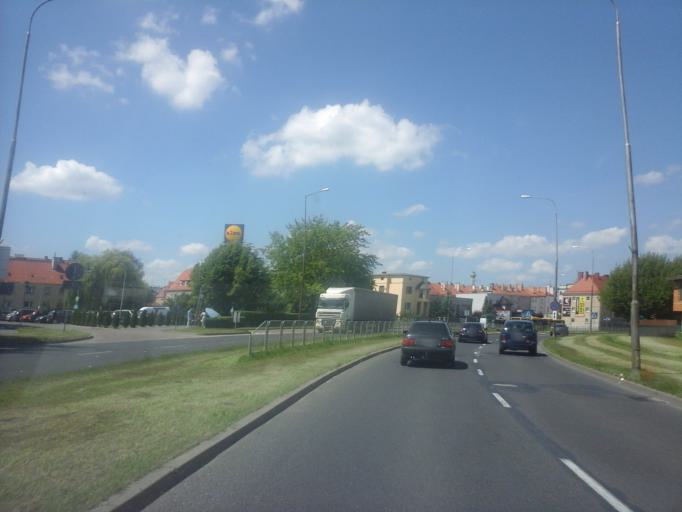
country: PL
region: West Pomeranian Voivodeship
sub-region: Koszalin
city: Koszalin
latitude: 54.1834
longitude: 16.1808
